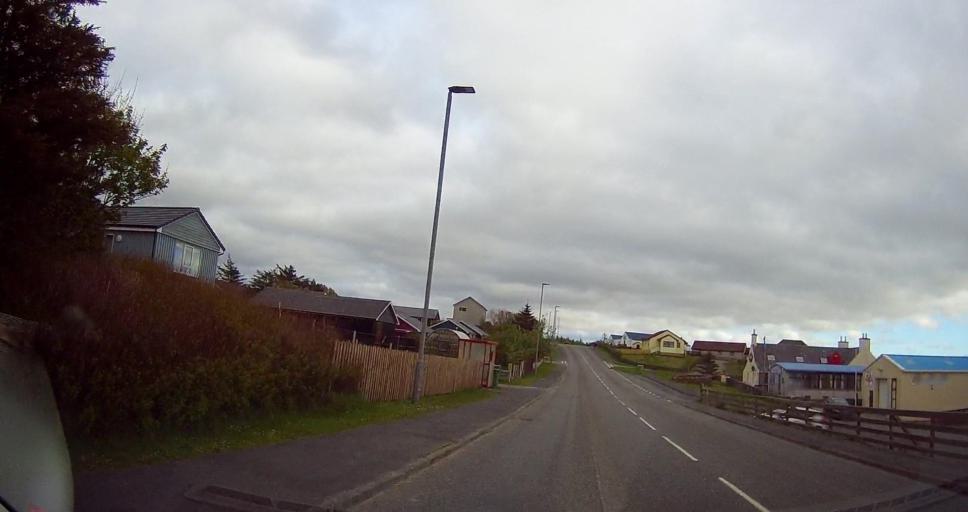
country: GB
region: Scotland
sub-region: Shetland Islands
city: Lerwick
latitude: 60.3900
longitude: -1.3488
